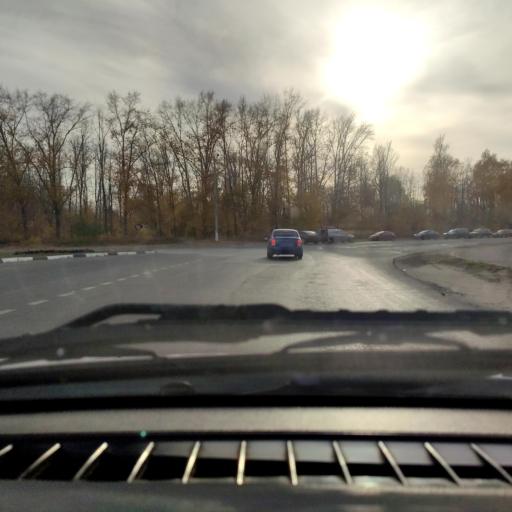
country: RU
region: Samara
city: Tol'yatti
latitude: 53.4960
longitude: 49.2890
